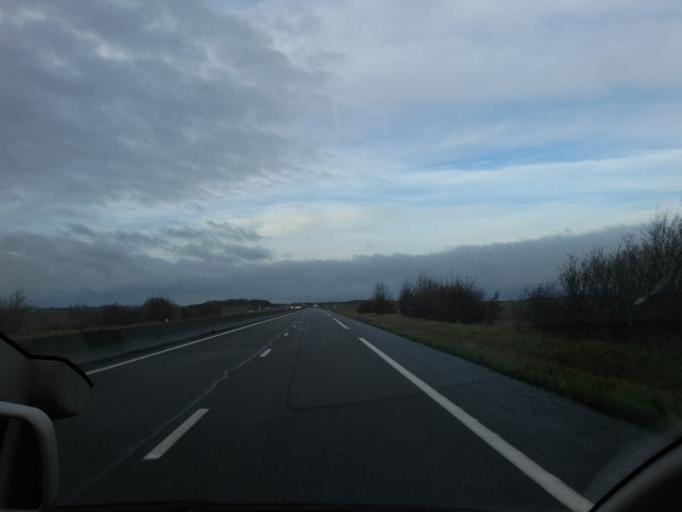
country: FR
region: Picardie
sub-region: Departement de la Somme
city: Harbonnieres
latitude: 49.8579
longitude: 2.6954
